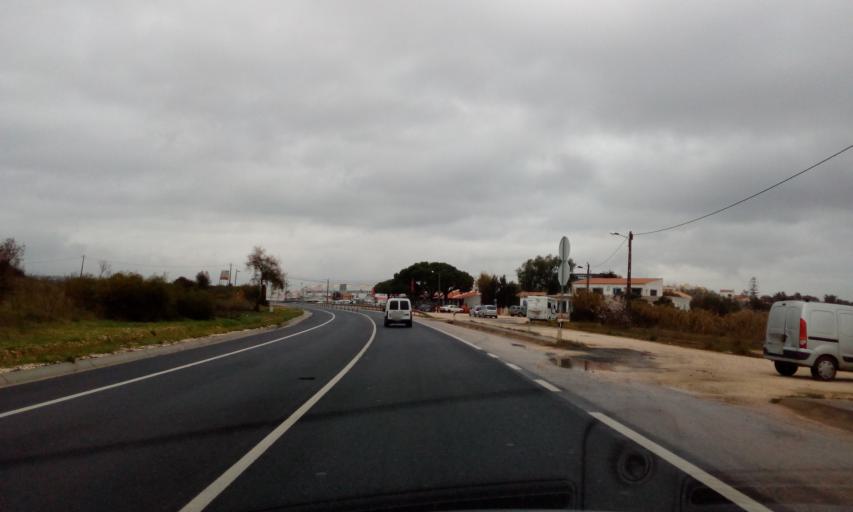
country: PT
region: Faro
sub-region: Lagos
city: Lagos
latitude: 37.1341
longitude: -8.6644
